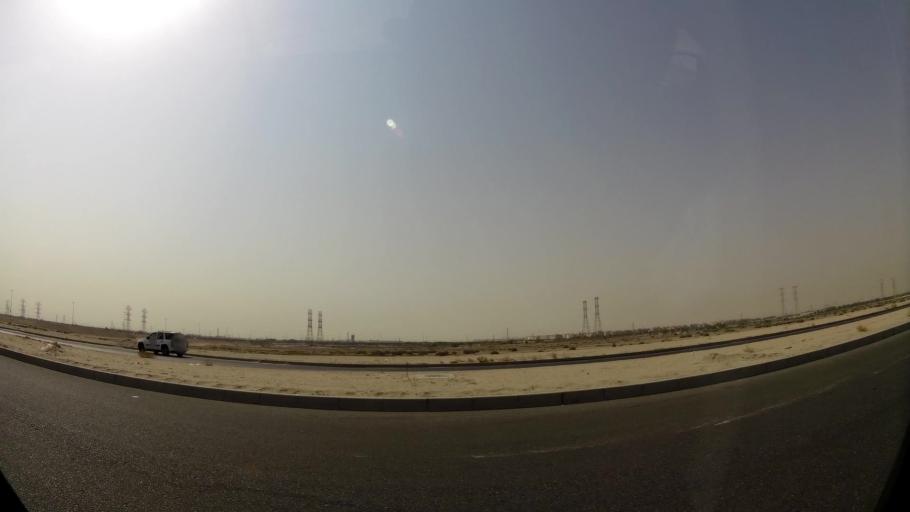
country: KW
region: Muhafazat al Jahra'
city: Al Jahra'
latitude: 29.3347
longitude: 47.7548
